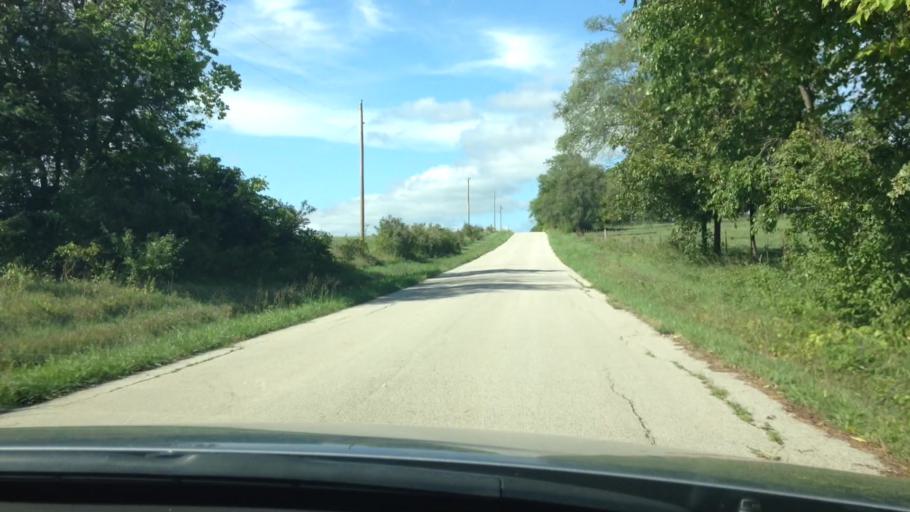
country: US
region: Missouri
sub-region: Platte County
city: Weatherby Lake
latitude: 39.3344
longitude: -94.6675
